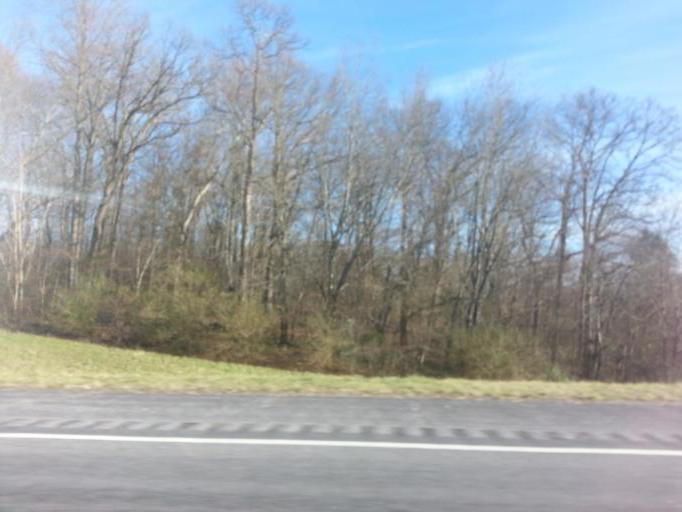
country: US
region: Tennessee
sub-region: Warren County
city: McMinnville
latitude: 35.7328
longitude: -85.6628
